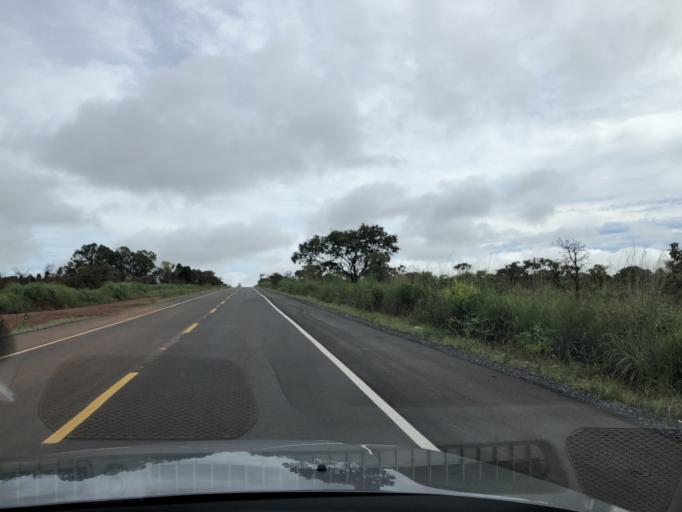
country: BR
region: Federal District
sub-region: Brasilia
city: Brasilia
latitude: -15.6390
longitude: -48.0786
